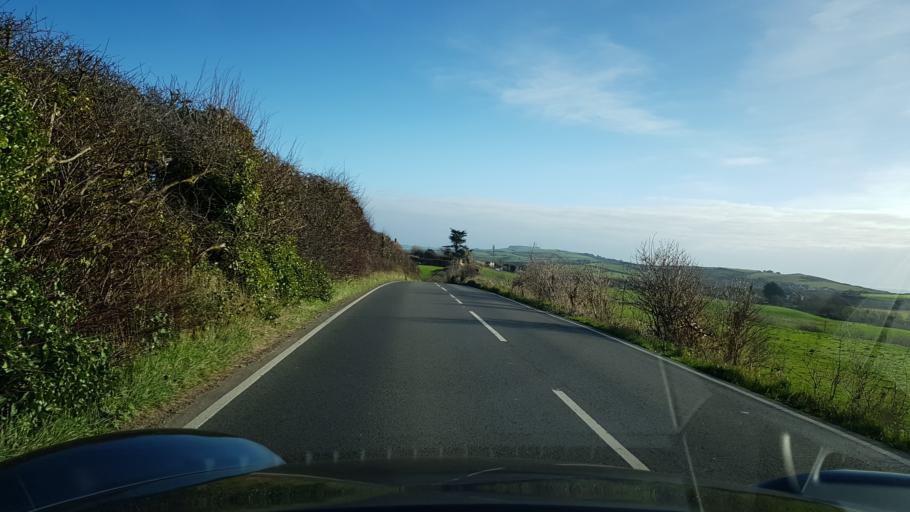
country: GB
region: England
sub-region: Dorset
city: Bridport
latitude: 50.7085
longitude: -2.7386
